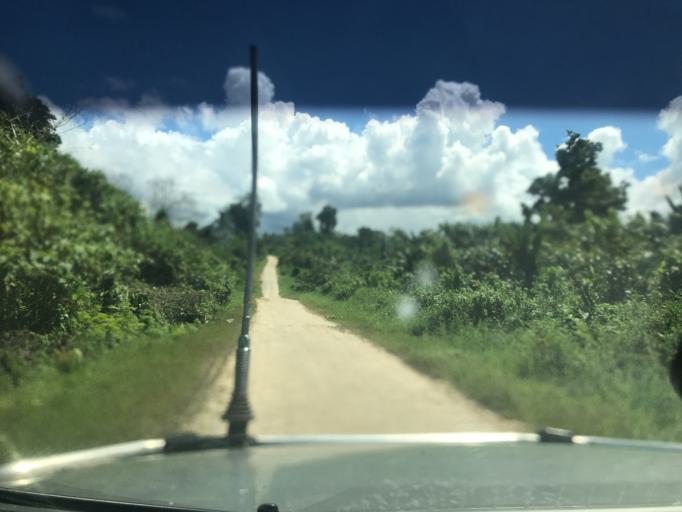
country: SB
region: Malaita
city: Auki
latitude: -8.7294
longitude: 160.9085
